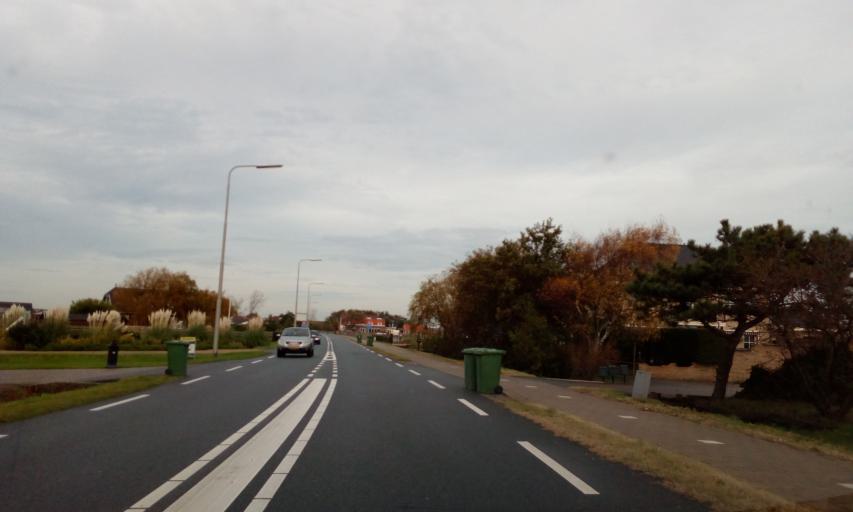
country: NL
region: South Holland
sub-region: Gemeente Rotterdam
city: Hoek van Holland
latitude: 51.9964
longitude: 4.1430
